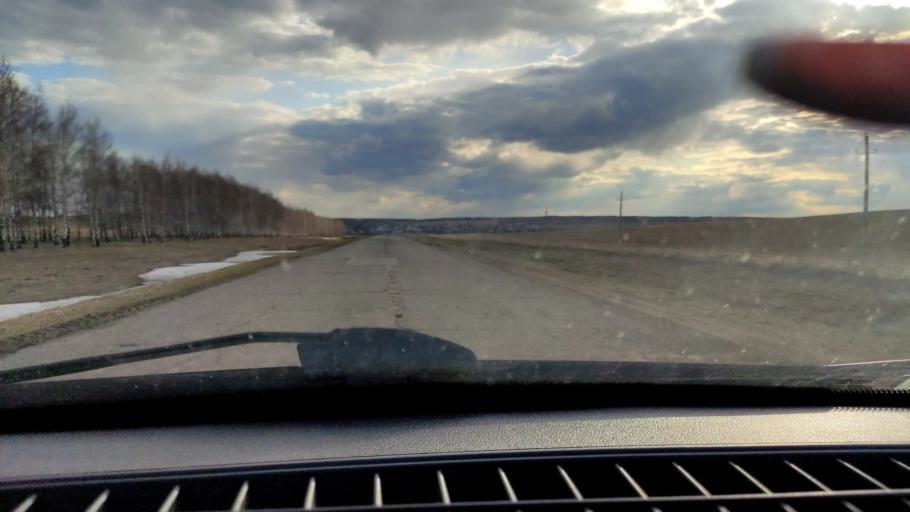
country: RU
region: Bashkortostan
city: Karmaskaly
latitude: 54.3449
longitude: 56.0232
